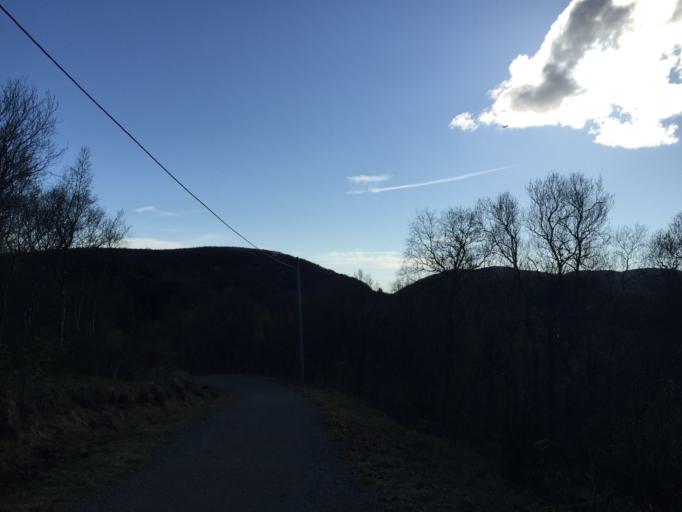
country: NO
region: Nordland
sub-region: Bodo
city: Lopsmarka
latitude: 67.2928
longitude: 14.5482
